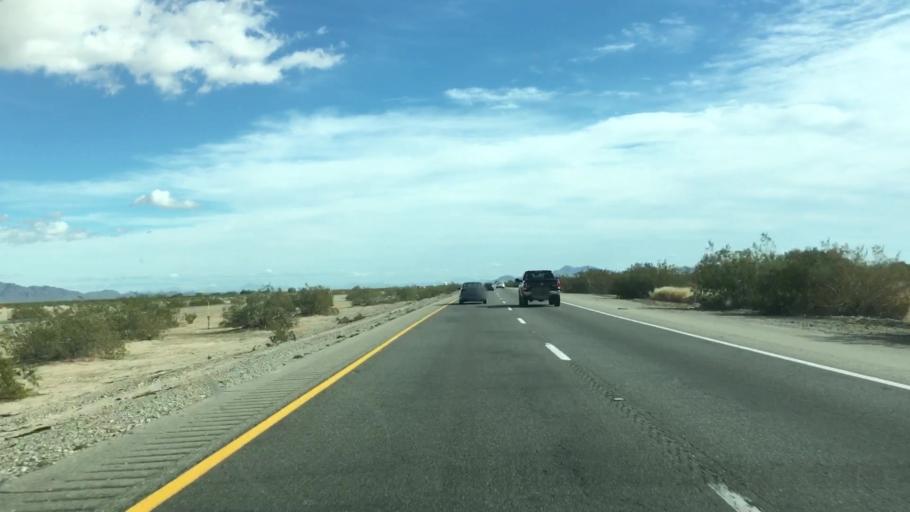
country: US
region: California
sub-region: Riverside County
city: Mesa Verde
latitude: 33.6202
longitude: -115.0337
